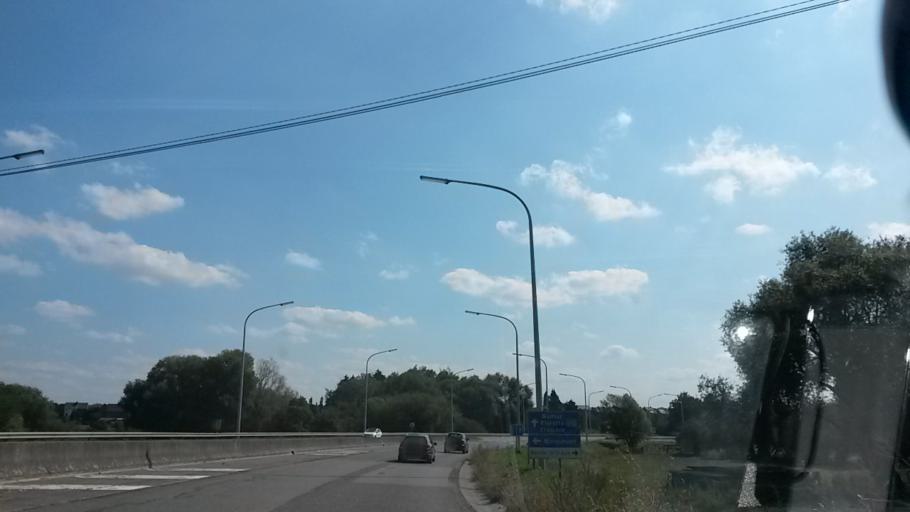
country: BE
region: Wallonia
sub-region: Province de Namur
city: Fosses-la-Ville
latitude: 50.4605
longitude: 4.6979
